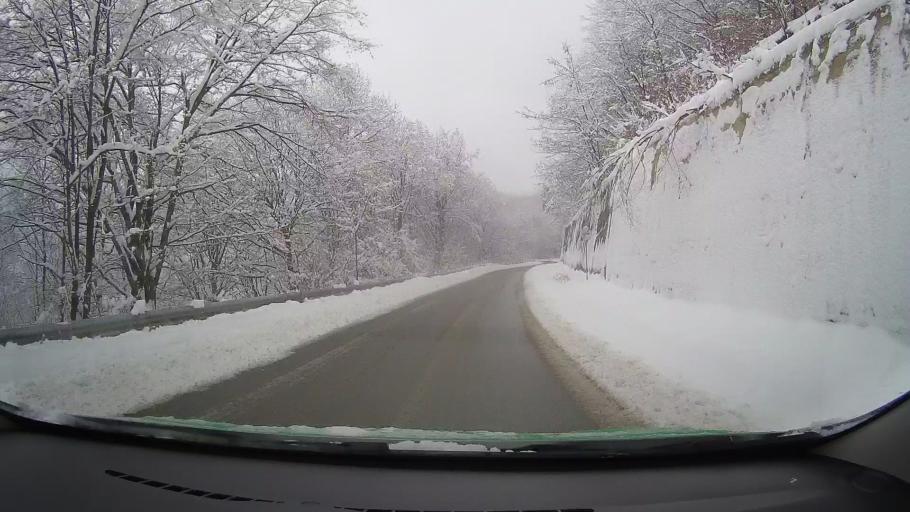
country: RO
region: Alba
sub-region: Comuna Sugag
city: Dobra
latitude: 45.7644
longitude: 23.6657
